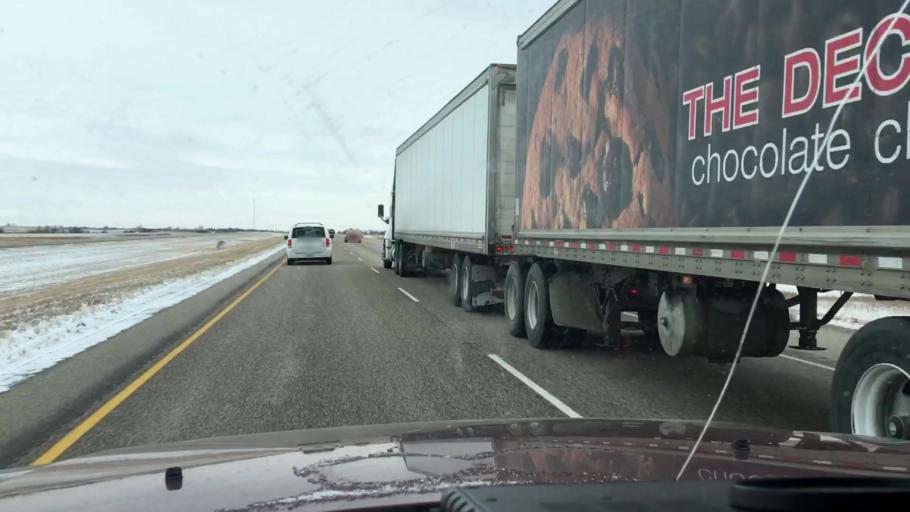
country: CA
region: Saskatchewan
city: Saskatoon
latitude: 51.5182
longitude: -106.2900
